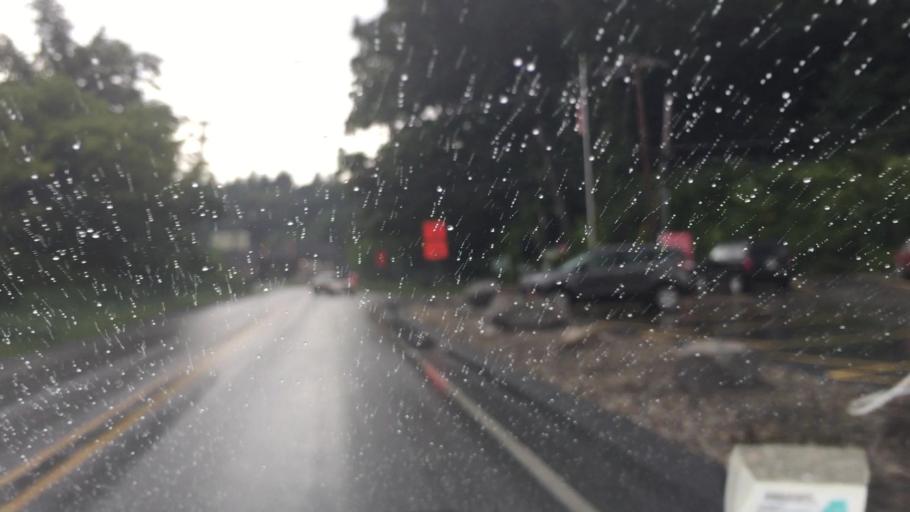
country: US
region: Pennsylvania
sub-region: Allegheny County
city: Millvale
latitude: 40.4993
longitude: -79.9797
